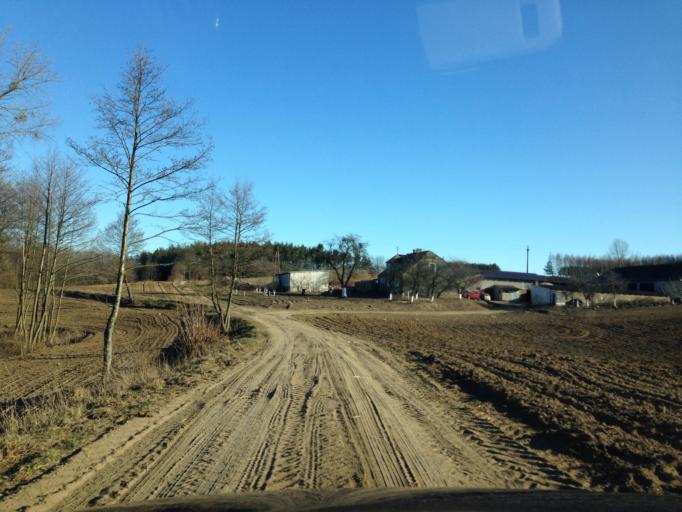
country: PL
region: Kujawsko-Pomorskie
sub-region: Powiat brodnicki
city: Brzozie
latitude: 53.3072
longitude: 19.6560
